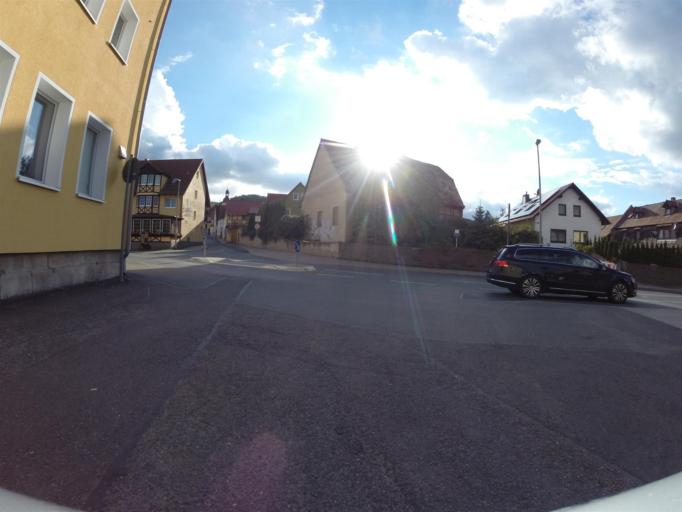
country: DE
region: Thuringia
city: Jena
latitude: 50.8922
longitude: 11.5852
